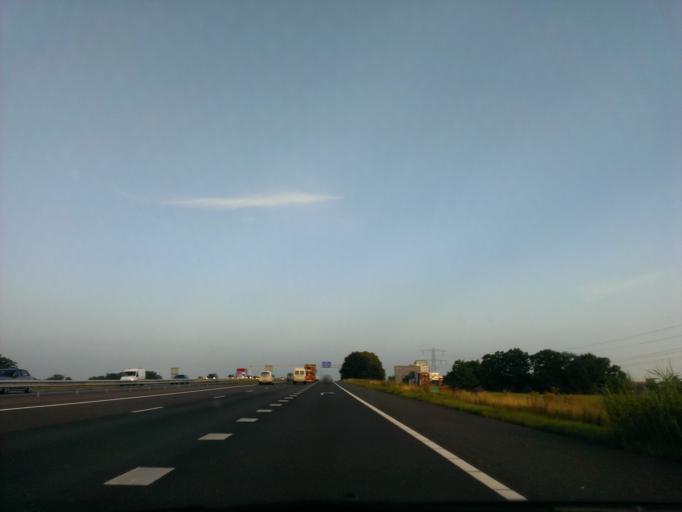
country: NL
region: Overijssel
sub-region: Gemeente Almelo
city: Almelo
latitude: 52.3216
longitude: 6.6584
